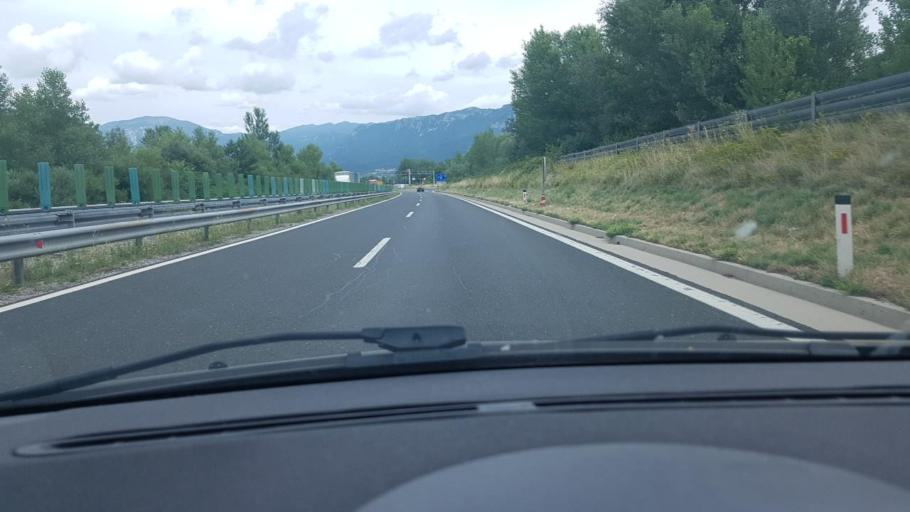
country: SI
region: Vipava
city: Vipava
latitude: 45.8245
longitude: 13.9605
